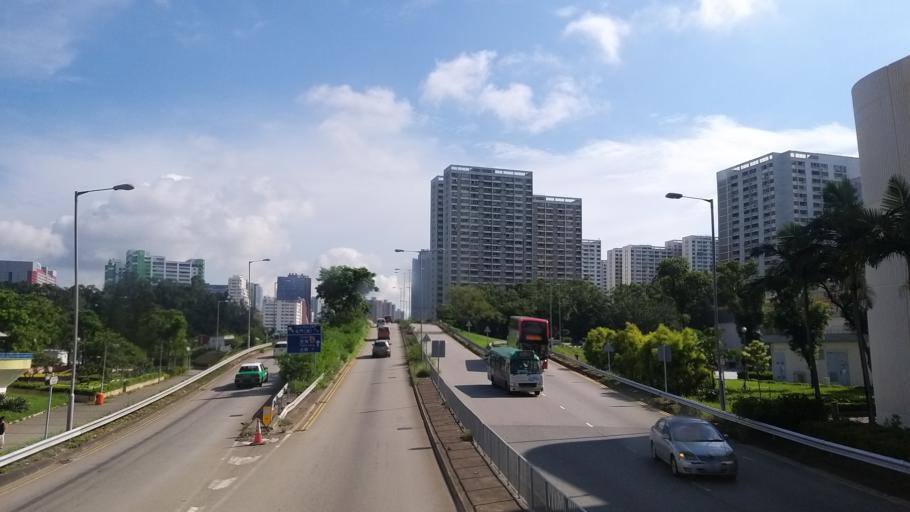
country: HK
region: Tuen Mun
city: Tuen Mun
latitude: 22.3846
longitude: 113.9707
